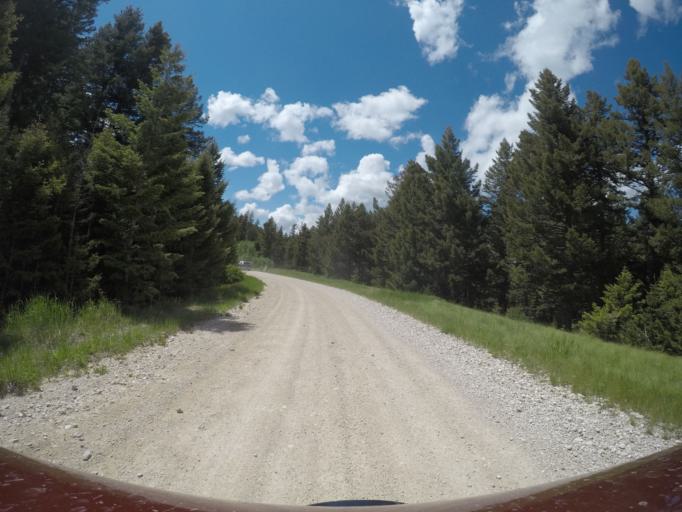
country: US
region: Wyoming
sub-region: Big Horn County
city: Lovell
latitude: 45.1993
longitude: -108.5004
